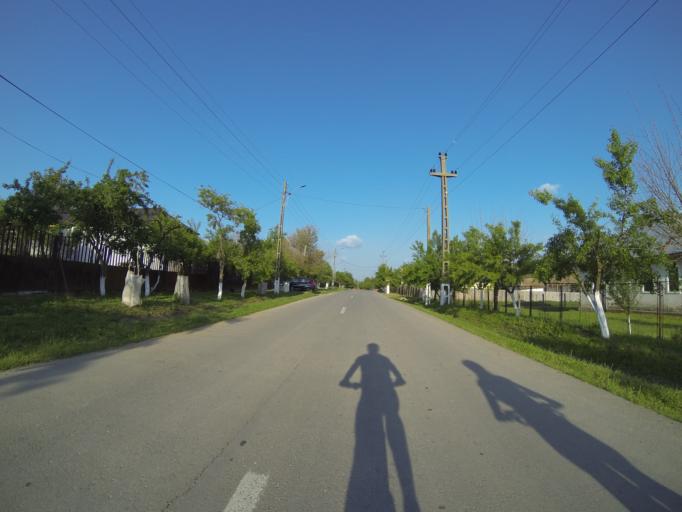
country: RO
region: Dolj
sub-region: Comuna Vela
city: Vela
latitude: 44.2680
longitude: 23.3857
